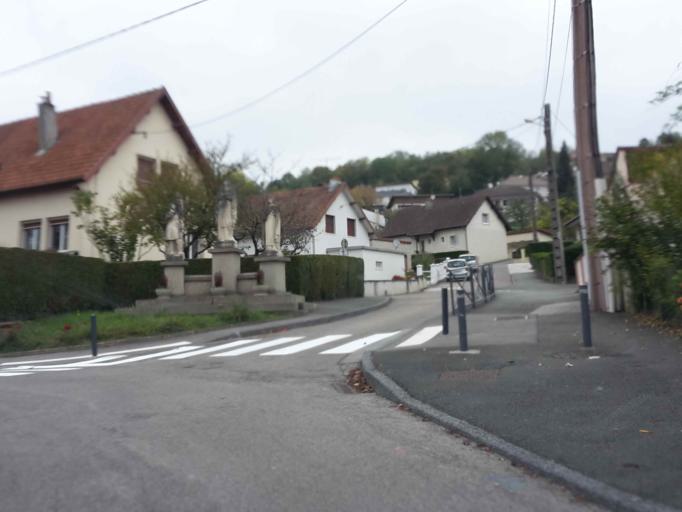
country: FR
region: Franche-Comte
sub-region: Departement du Doubs
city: Baume-les-Dames
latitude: 47.3445
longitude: 6.3660
